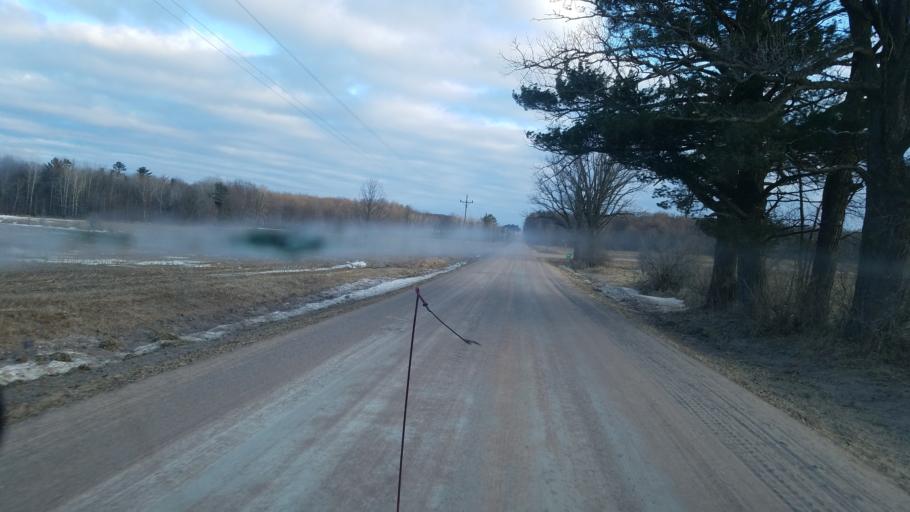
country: US
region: Wisconsin
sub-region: Clark County
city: Loyal
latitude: 44.6243
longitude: -90.4359
